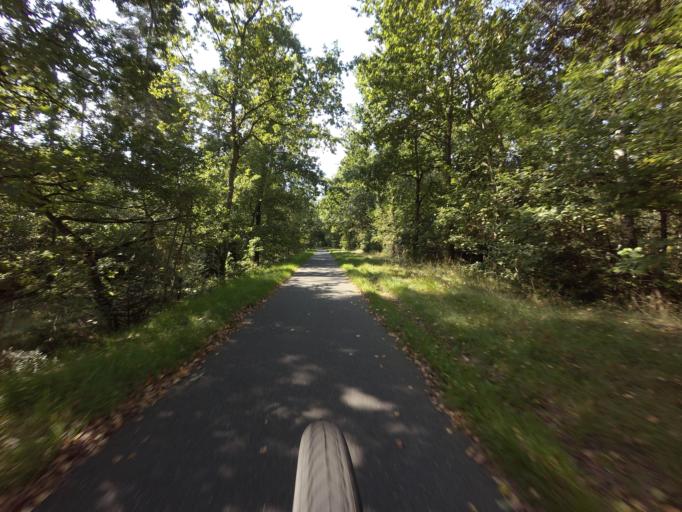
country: DK
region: Central Jutland
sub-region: Viborg Kommune
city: Viborg
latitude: 56.4138
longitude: 9.3644
